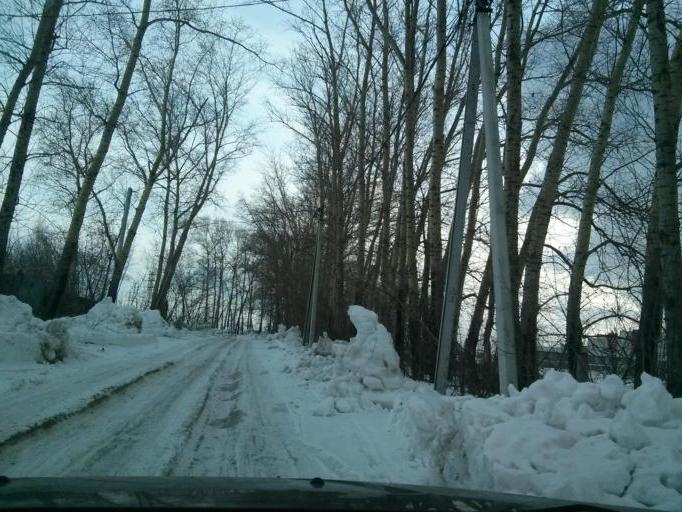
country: RU
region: Nizjnij Novgorod
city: Afonino
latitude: 56.2695
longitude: 44.0317
